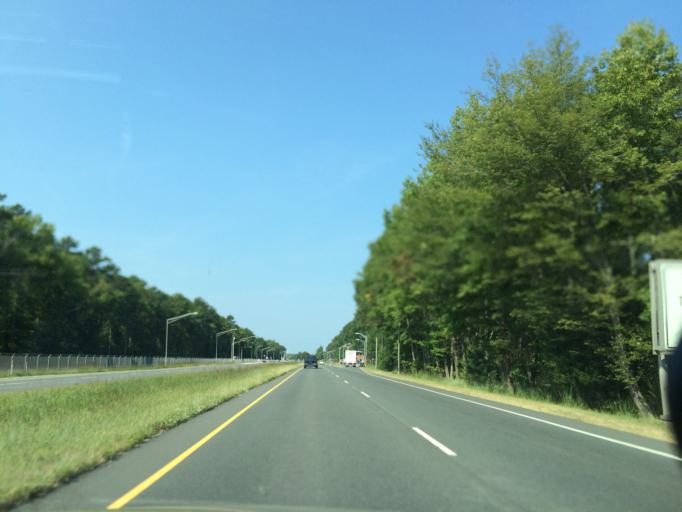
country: US
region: Virginia
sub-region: King George County
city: Dahlgren
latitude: 38.3579
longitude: -77.0279
